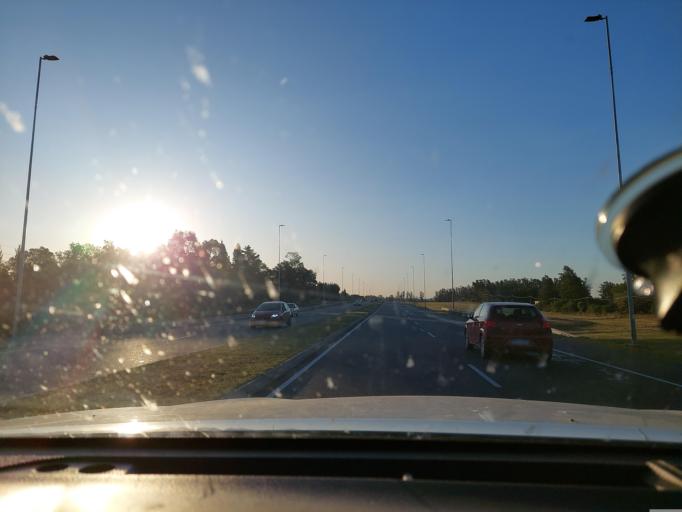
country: UY
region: Canelones
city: Empalme Olmos
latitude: -34.7010
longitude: -55.9053
